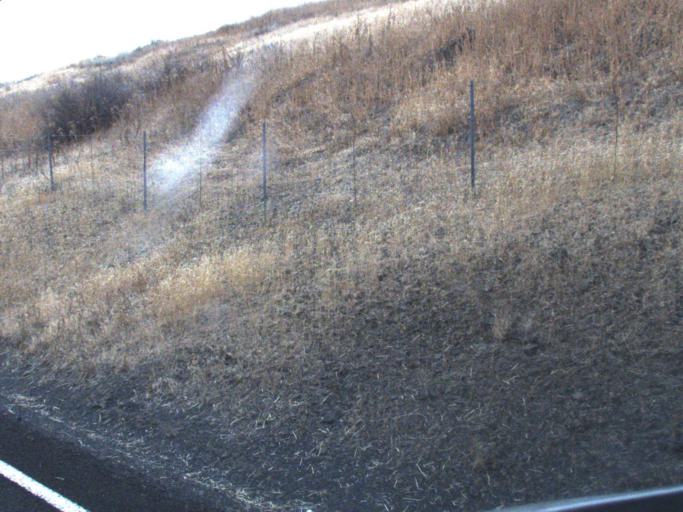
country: US
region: Washington
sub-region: Okanogan County
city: Coulee Dam
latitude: 47.8449
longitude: -118.7165
